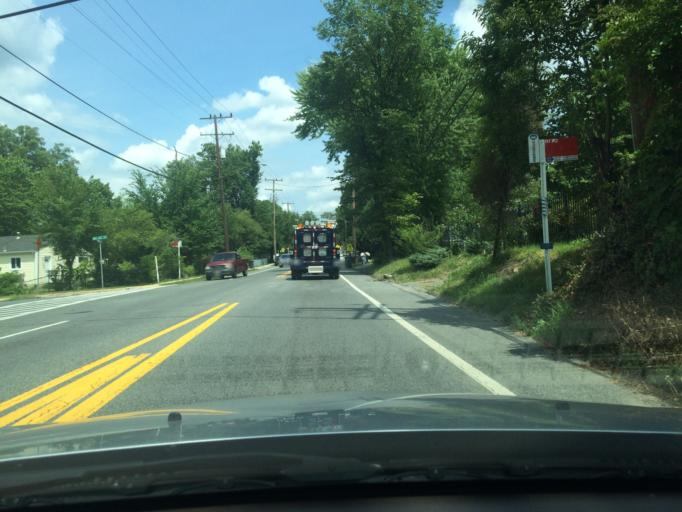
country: US
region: Maryland
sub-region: Prince George's County
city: Adelphi
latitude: 38.9955
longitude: -76.9721
